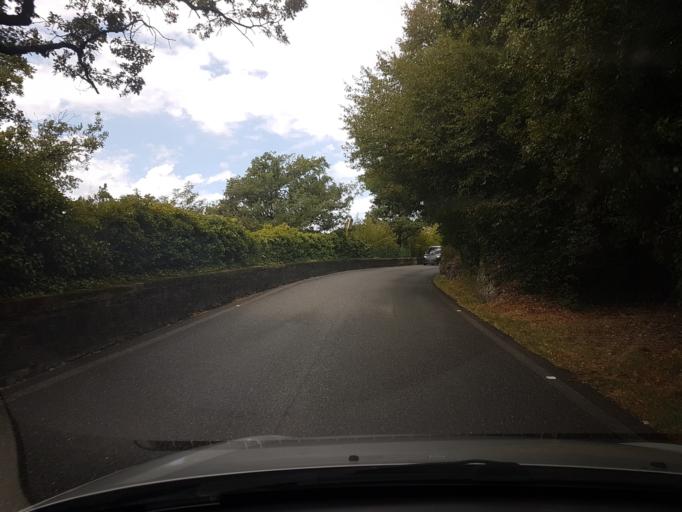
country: IT
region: Friuli Venezia Giulia
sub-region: Provincia di Trieste
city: Prosecco-Contovello
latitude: 45.6983
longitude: 13.7383
